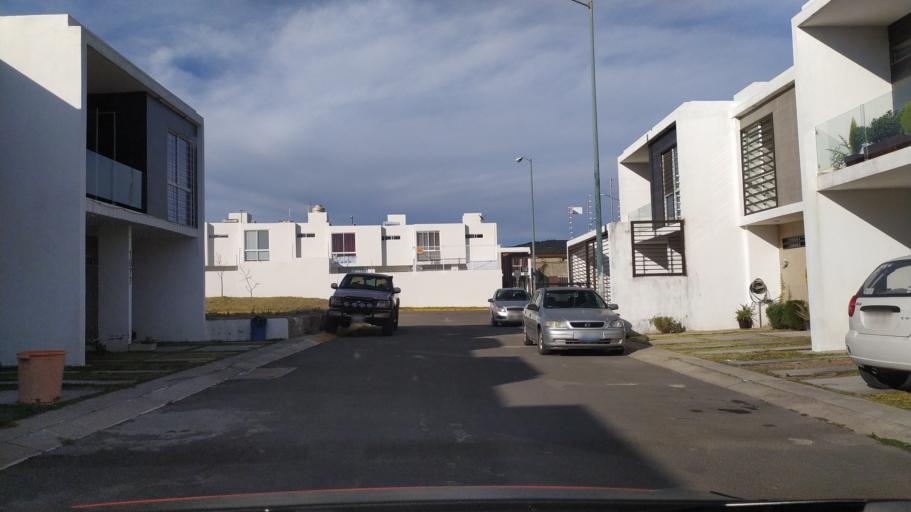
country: MX
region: Jalisco
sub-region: Tlajomulco de Zuniga
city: Palomar
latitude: 20.6327
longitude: -103.4812
